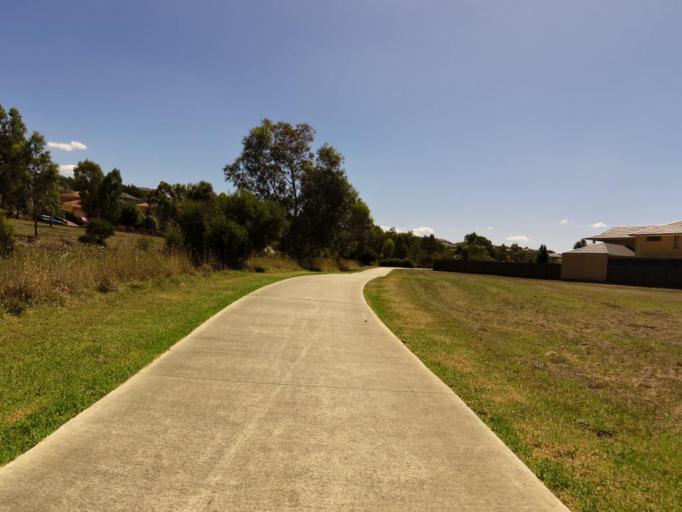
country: AU
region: Victoria
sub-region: Hume
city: Meadow Heights
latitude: -37.6496
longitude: 144.9080
